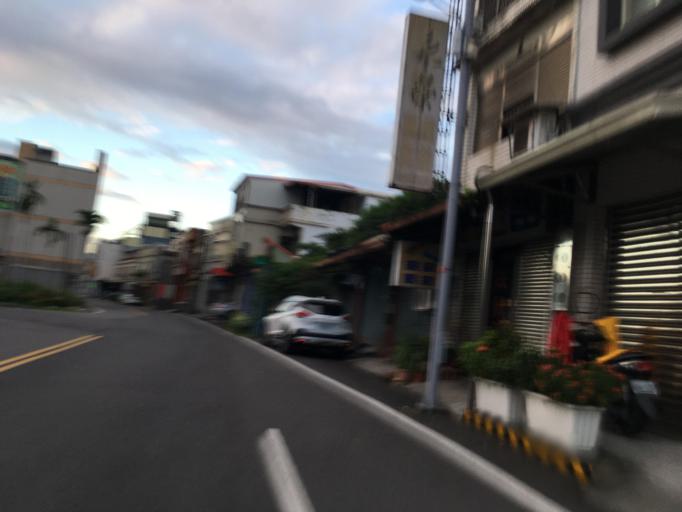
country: TW
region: Taiwan
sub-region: Yilan
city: Yilan
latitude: 24.6236
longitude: 121.8344
